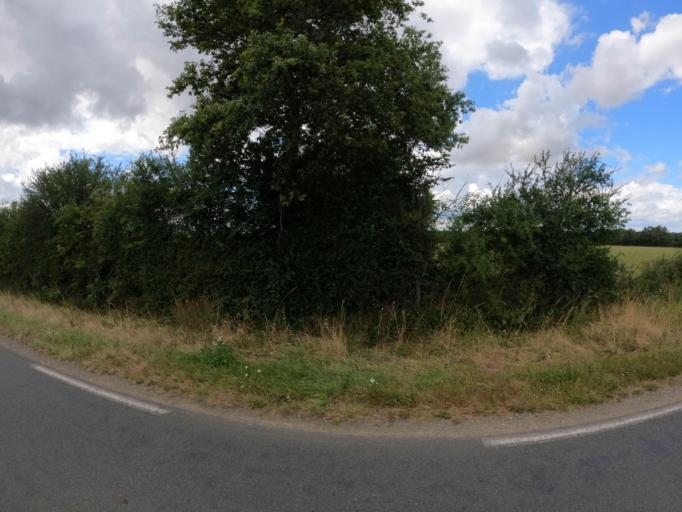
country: FR
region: Pays de la Loire
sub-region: Departement de la Sarthe
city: Solesmes
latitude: 47.8641
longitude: -0.3148
